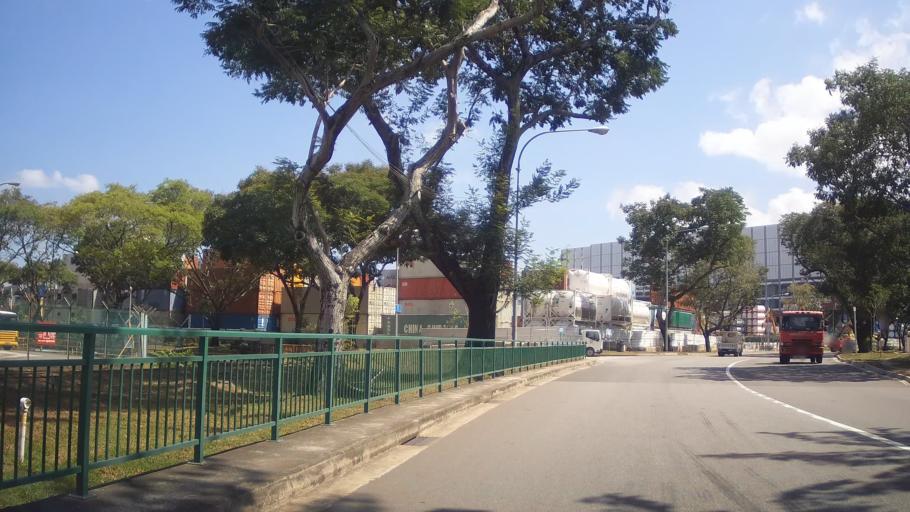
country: SG
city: Singapore
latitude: 1.3065
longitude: 103.6931
